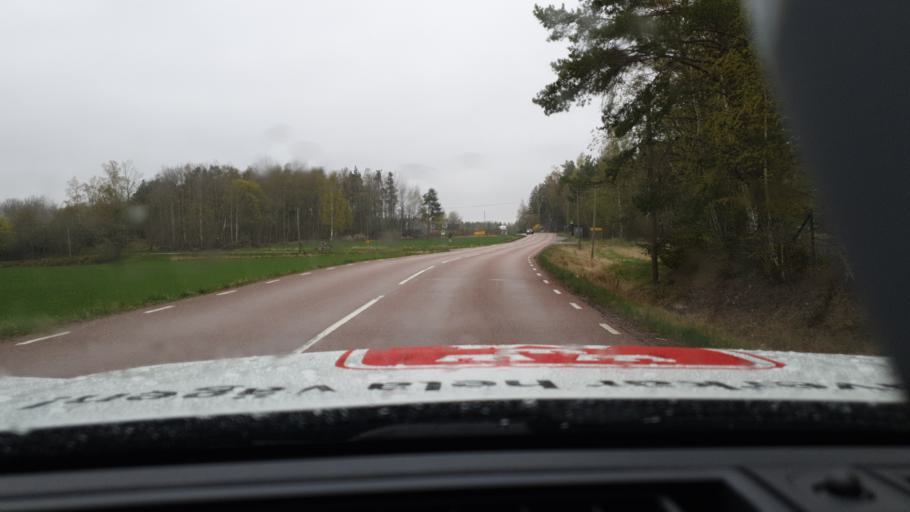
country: SE
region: Soedermanland
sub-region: Strangnas Kommun
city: Stallarholmen
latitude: 59.3304
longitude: 17.2236
